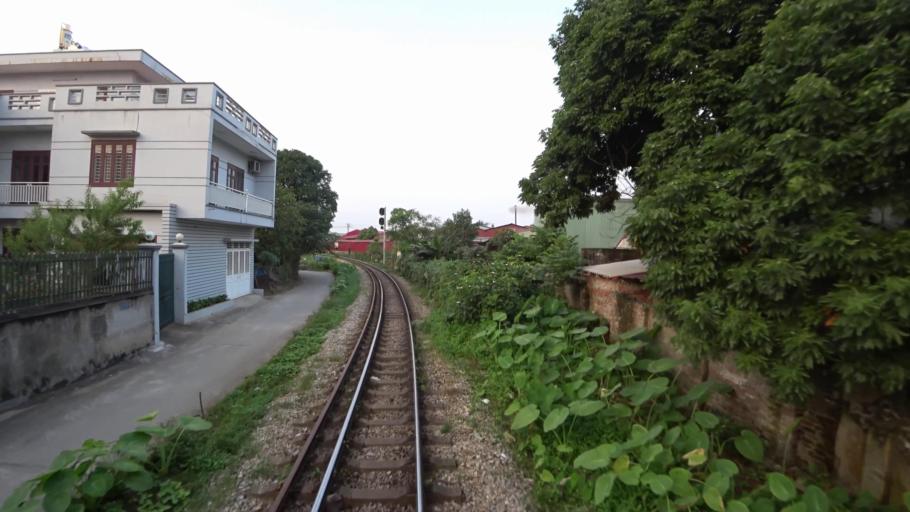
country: VN
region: Ha Noi
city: Dong Anh
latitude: 21.1079
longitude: 105.8989
